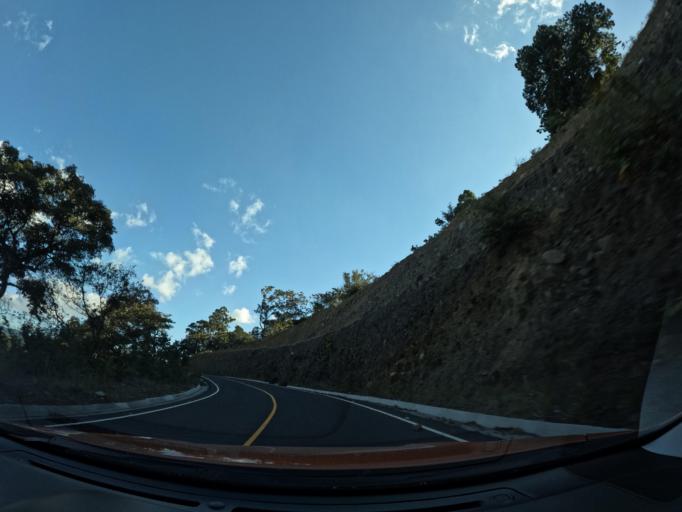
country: GT
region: Escuintla
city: Palin
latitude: 14.4437
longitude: -90.6945
